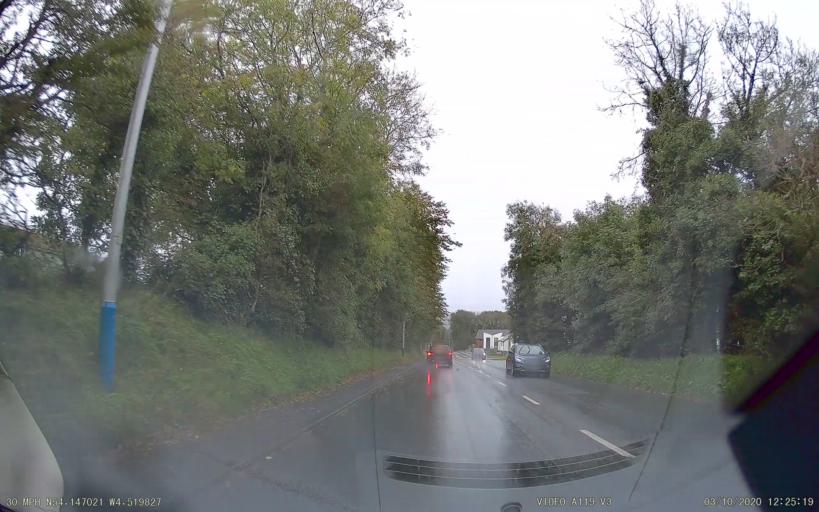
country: IM
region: Douglas
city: Douglas
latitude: 54.1470
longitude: -4.5198
